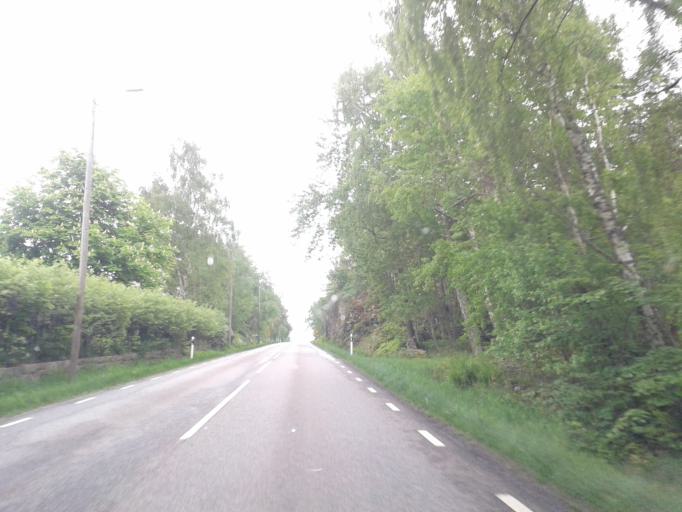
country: SE
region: Vaestra Goetaland
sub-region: Kungalvs Kommun
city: Kode
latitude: 57.8965
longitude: 11.7348
